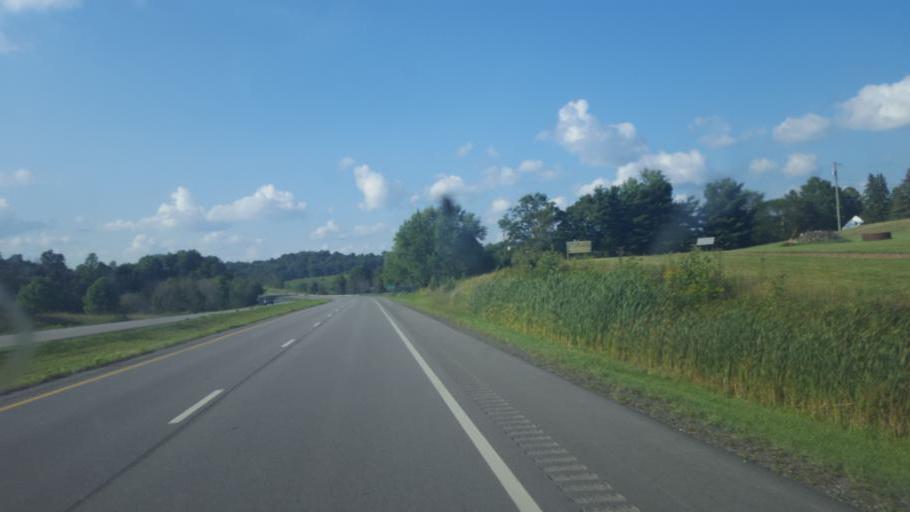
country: US
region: Ohio
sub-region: Sandusky County
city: Bellville
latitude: 40.6566
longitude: -82.5131
